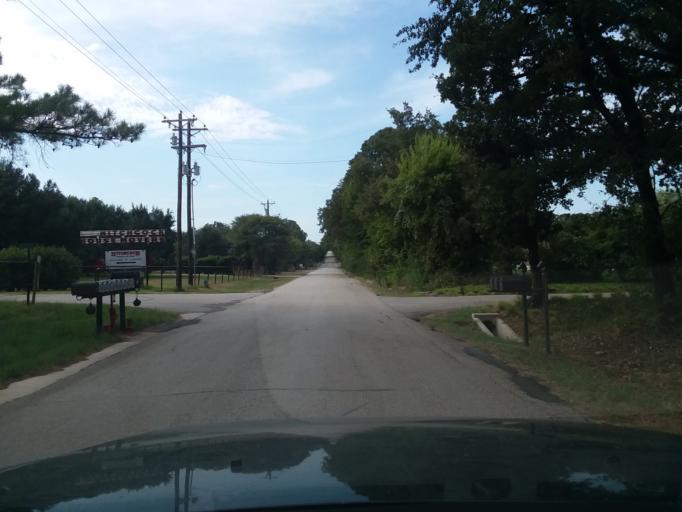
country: US
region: Texas
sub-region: Denton County
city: Bartonville
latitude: 33.1103
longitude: -97.1311
